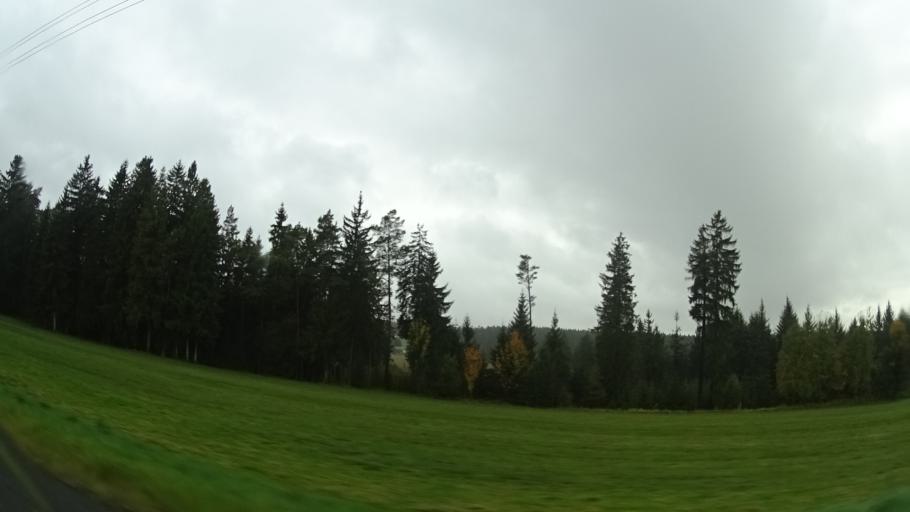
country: DE
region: Thuringia
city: Wurzbach
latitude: 50.4474
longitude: 11.5241
